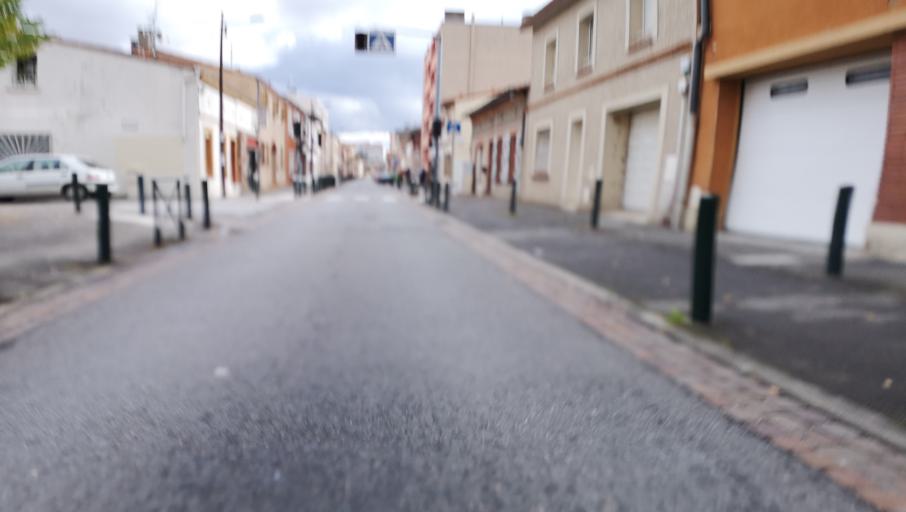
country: FR
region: Midi-Pyrenees
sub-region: Departement de la Haute-Garonne
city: Toulouse
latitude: 43.6018
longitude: 1.4160
